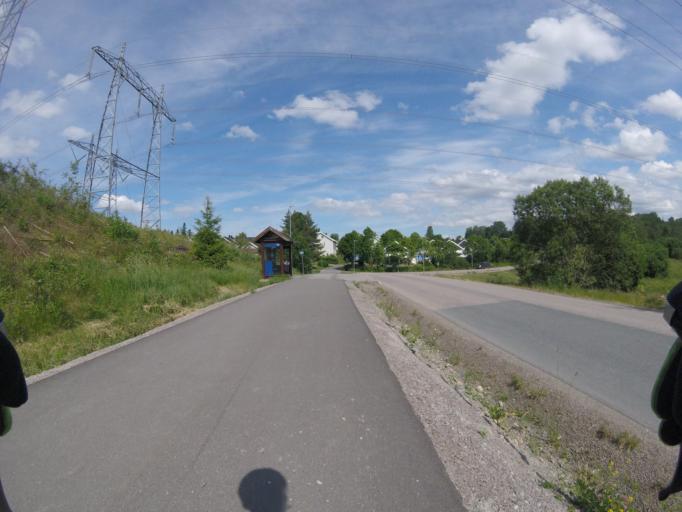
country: NO
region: Akershus
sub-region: Skedsmo
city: Lillestrom
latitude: 59.9891
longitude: 11.0363
